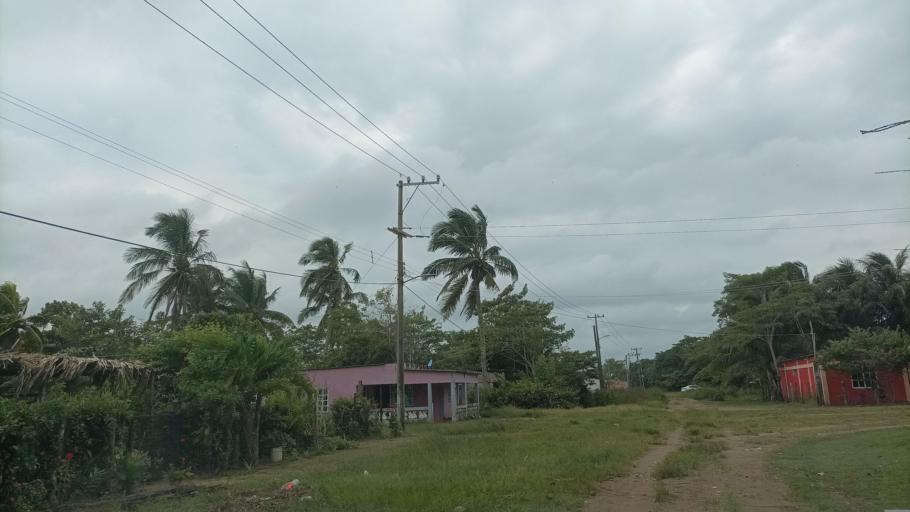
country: MX
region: Veracruz
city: Agua Dulce
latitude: 18.2069
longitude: -94.1397
